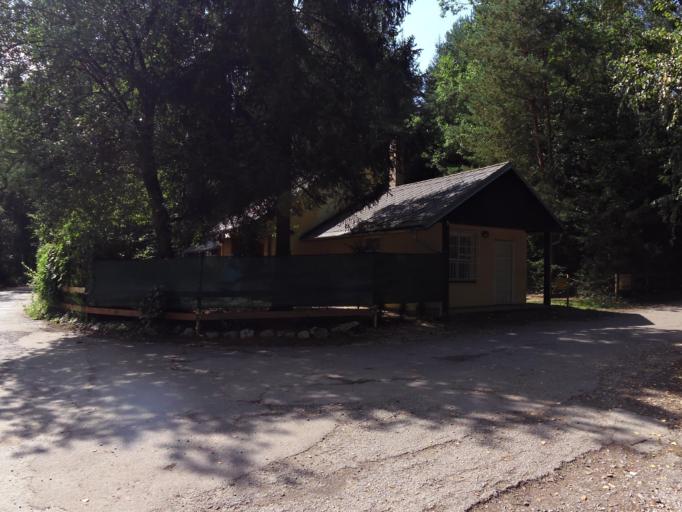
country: CZ
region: Jihocesky
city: Chlum u Trebone
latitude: 48.9845
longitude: 14.9608
